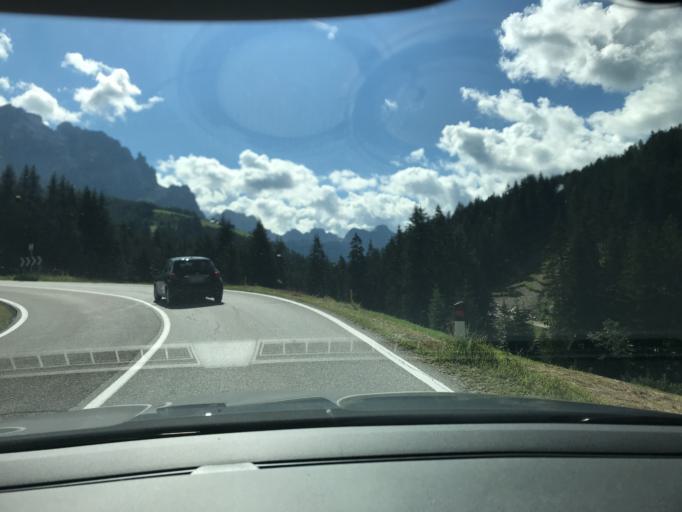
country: IT
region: Trentino-Alto Adige
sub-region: Bolzano
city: Badia
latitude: 46.5831
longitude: 11.9102
